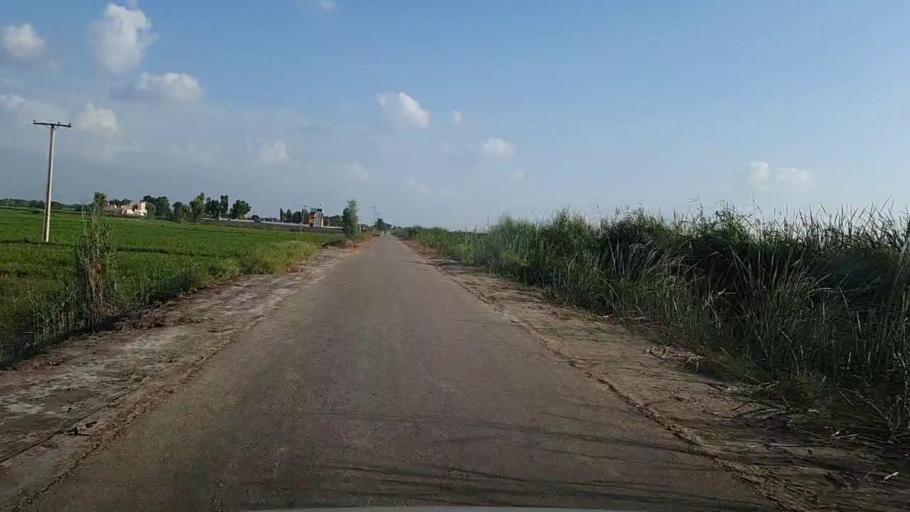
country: PK
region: Sindh
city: Hingorja
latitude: 27.0921
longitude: 68.4025
